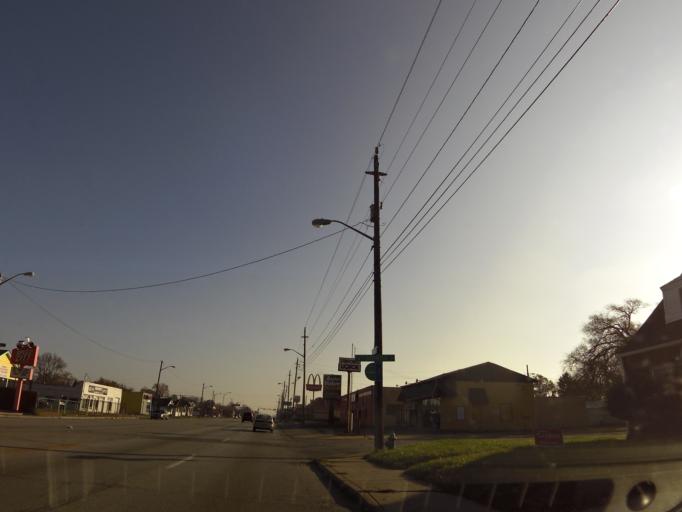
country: US
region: Indiana
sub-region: Marion County
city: Speedway
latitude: 39.7877
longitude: -86.2189
